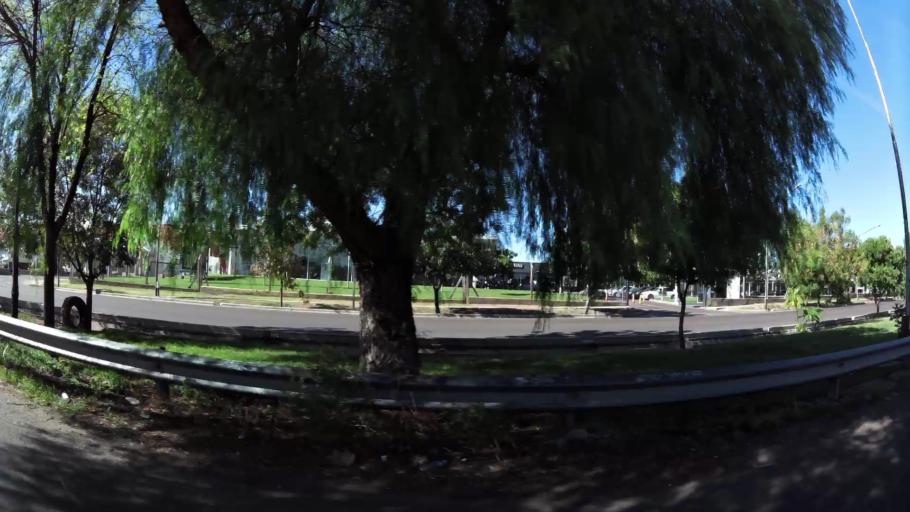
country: AR
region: Mendoza
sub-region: Departamento de Godoy Cruz
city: Godoy Cruz
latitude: -32.9260
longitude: -68.8316
